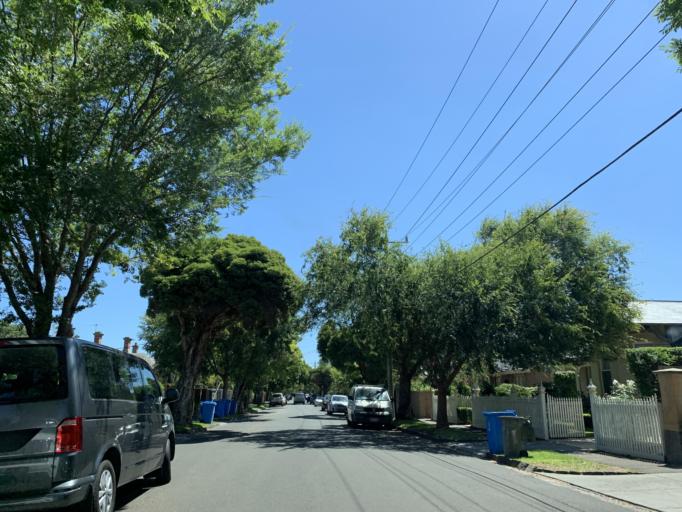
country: AU
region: Victoria
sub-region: Bayside
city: North Brighton
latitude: -37.9002
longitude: 144.9934
